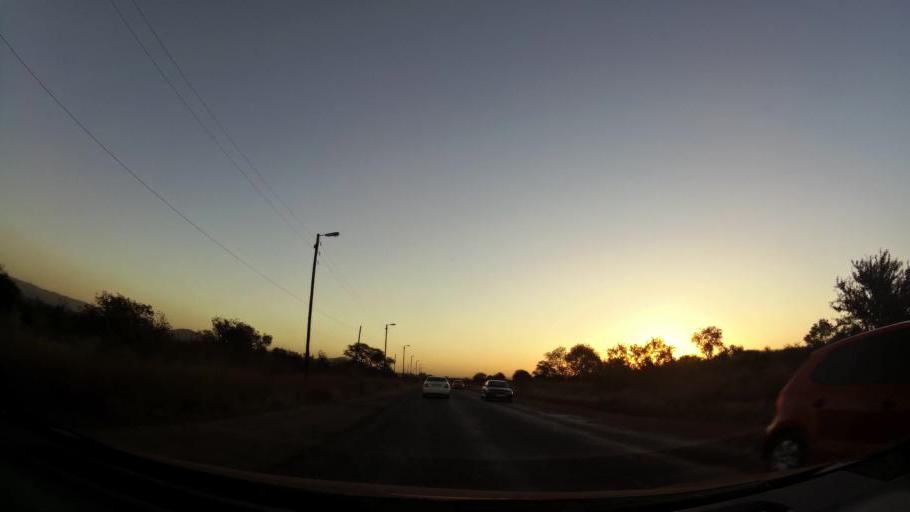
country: ZA
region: North-West
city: Ga-Rankuwa
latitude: -25.6204
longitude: 28.0333
